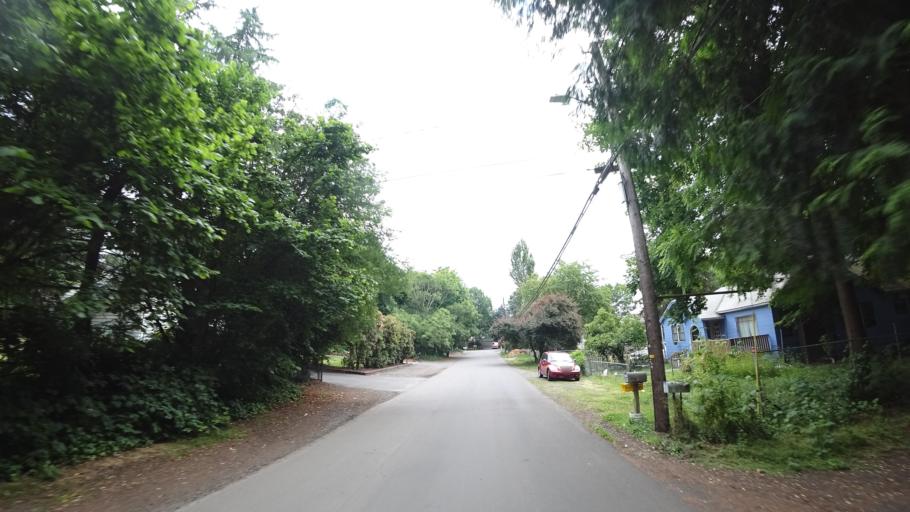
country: US
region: Oregon
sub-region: Multnomah County
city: Portland
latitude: 45.5686
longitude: -122.6182
